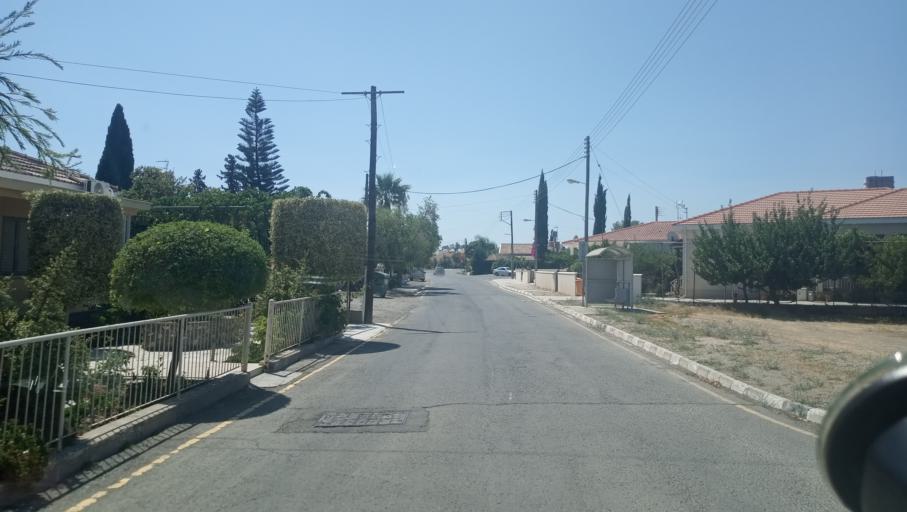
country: CY
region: Lefkosia
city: Psimolofou
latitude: 35.0656
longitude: 33.2596
